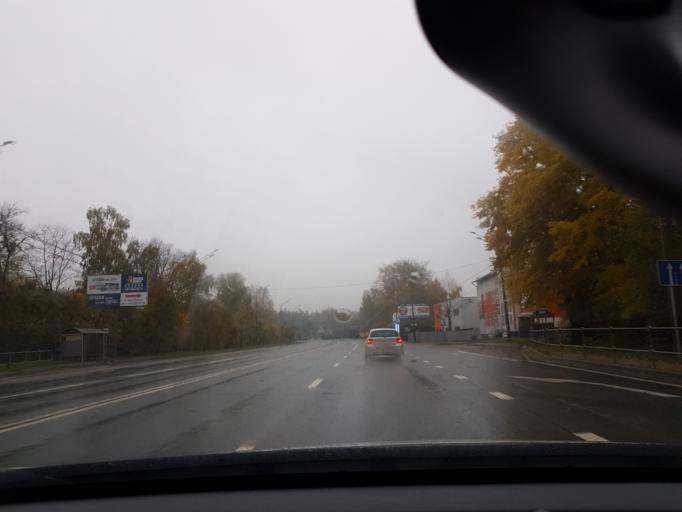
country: RU
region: Moskovskaya
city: Istra
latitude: 55.9044
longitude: 36.8953
